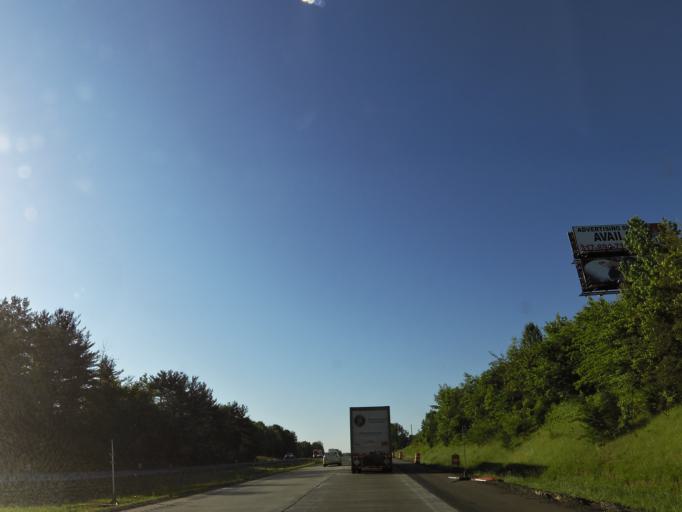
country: US
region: Indiana
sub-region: Jackson County
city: Seymour
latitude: 38.9015
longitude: -85.8204
